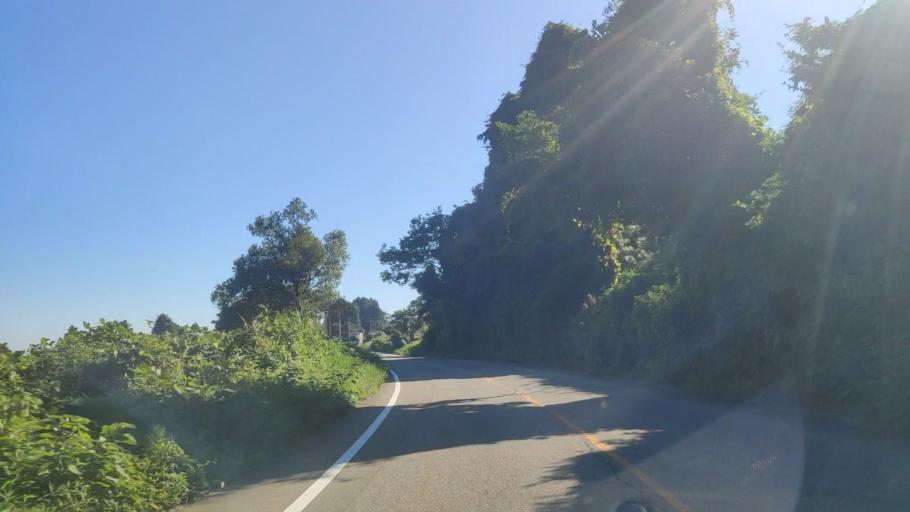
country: JP
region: Ishikawa
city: Nanao
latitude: 37.2711
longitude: 137.0949
